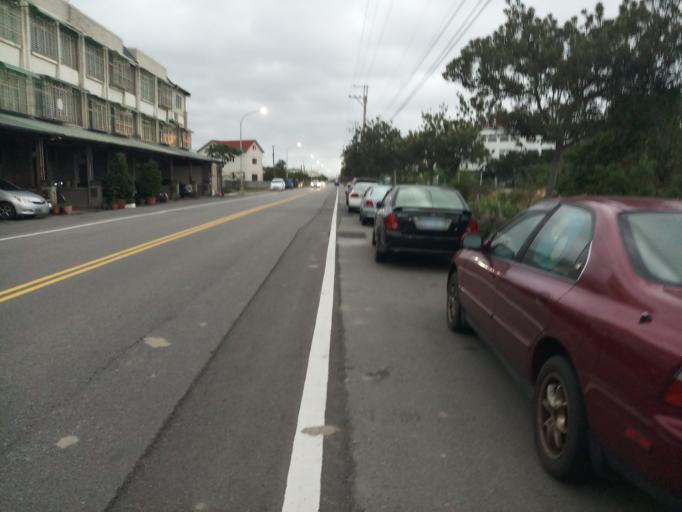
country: TW
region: Taiwan
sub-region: Miaoli
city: Miaoli
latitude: 24.6788
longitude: 120.8606
